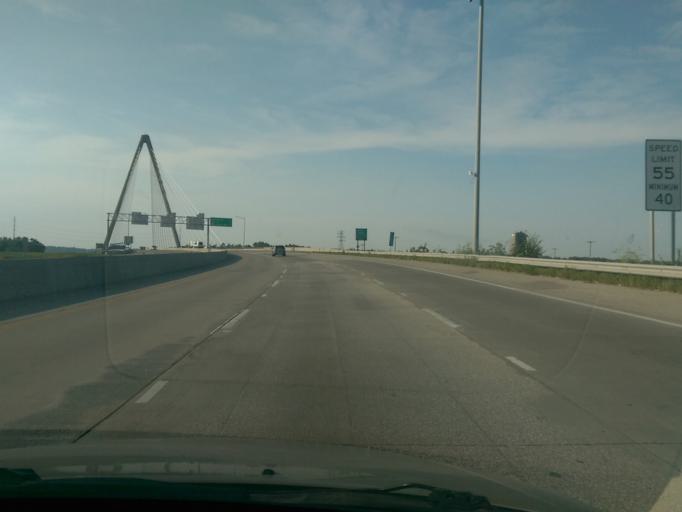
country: US
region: Missouri
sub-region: Clay County
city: North Kansas City
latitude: 39.1191
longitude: -94.5644
